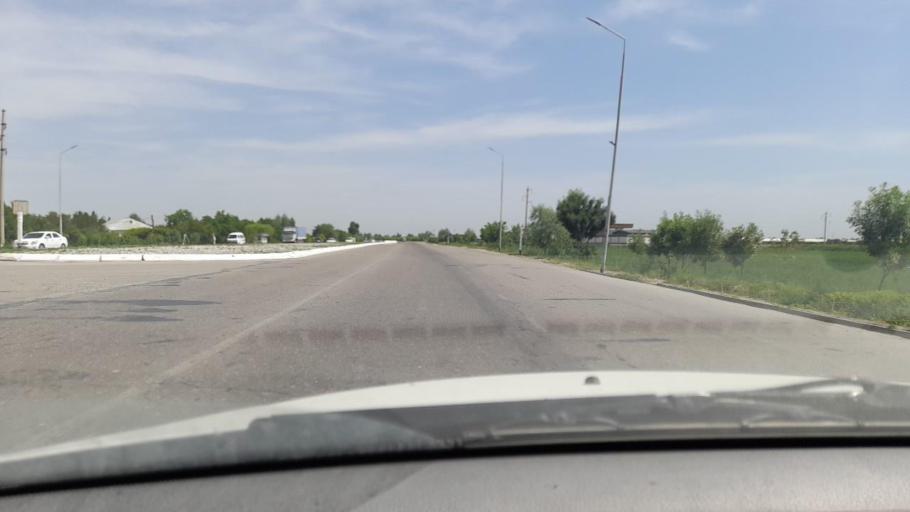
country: UZ
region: Bukhara
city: Galaosiyo
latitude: 39.8684
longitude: 64.4523
